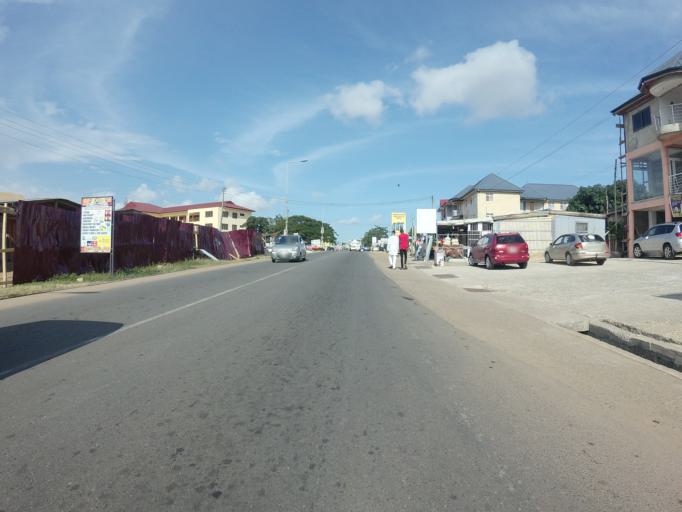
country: GH
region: Greater Accra
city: Medina Estates
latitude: 5.6417
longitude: -0.1688
